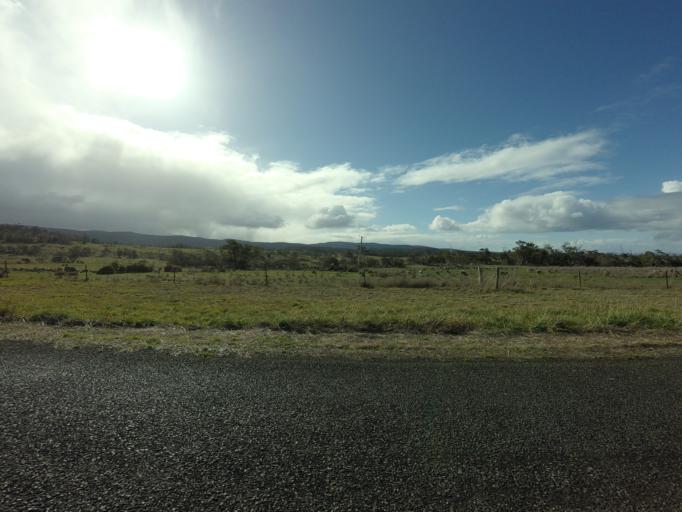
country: AU
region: Tasmania
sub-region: Sorell
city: Sorell
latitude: -42.3001
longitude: 147.9875
